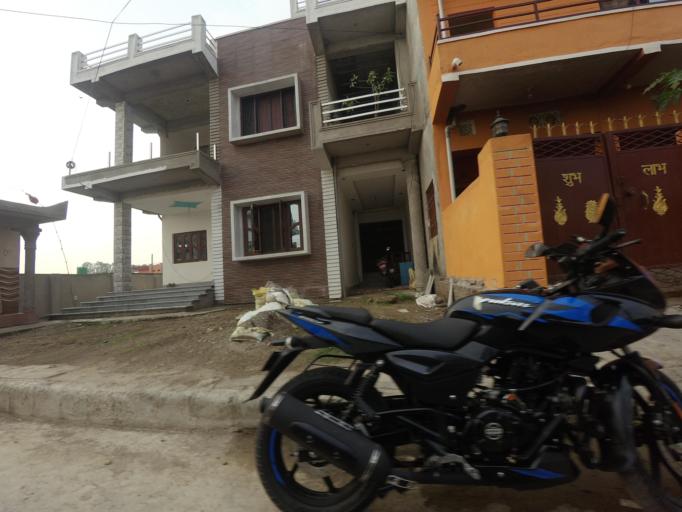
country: NP
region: Western Region
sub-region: Lumbini Zone
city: Bhairahawa
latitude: 27.5023
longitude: 83.4457
